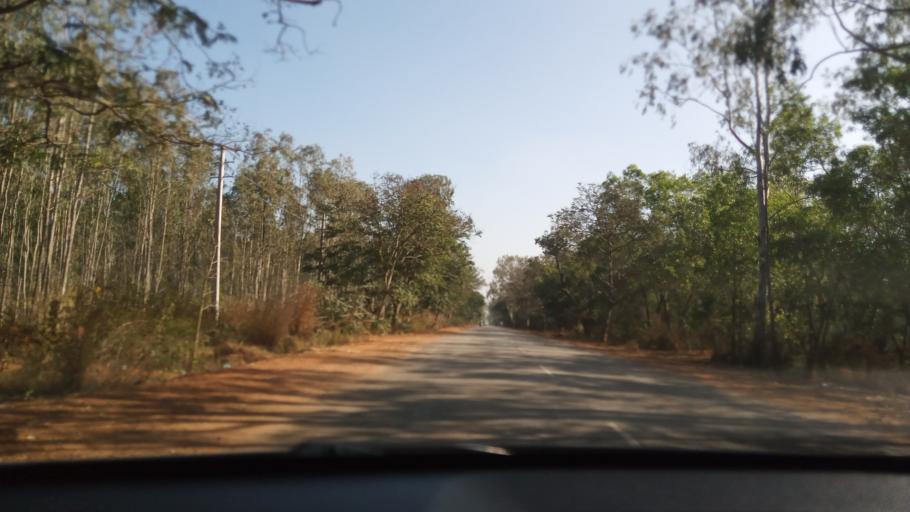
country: IN
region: Karnataka
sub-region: Bangalore Rural
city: Devanhalli
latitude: 13.2705
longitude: 77.7473
